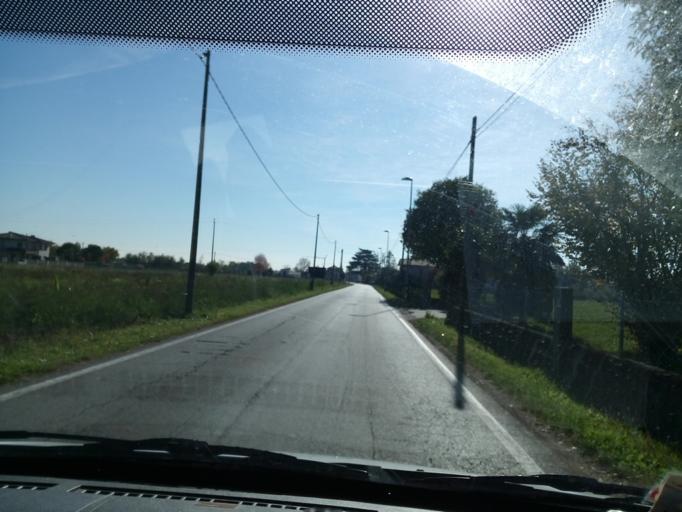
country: IT
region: Veneto
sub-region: Provincia di Treviso
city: Ramon
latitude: 45.7110
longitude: 11.8436
